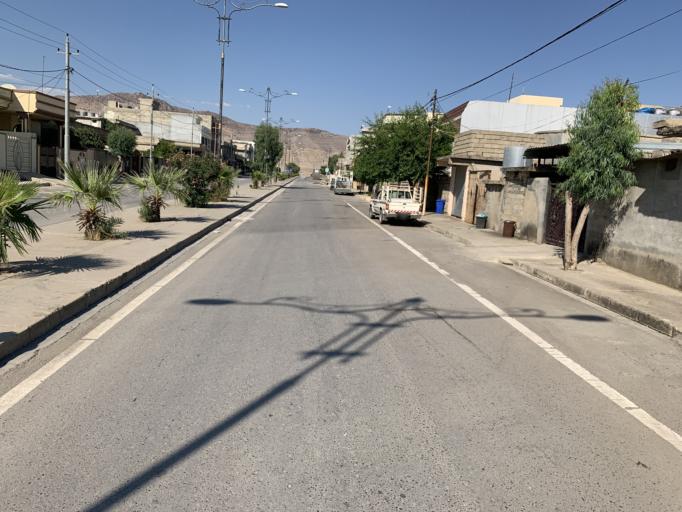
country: IQ
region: As Sulaymaniyah
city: Raniye
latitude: 36.2366
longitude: 44.7970
